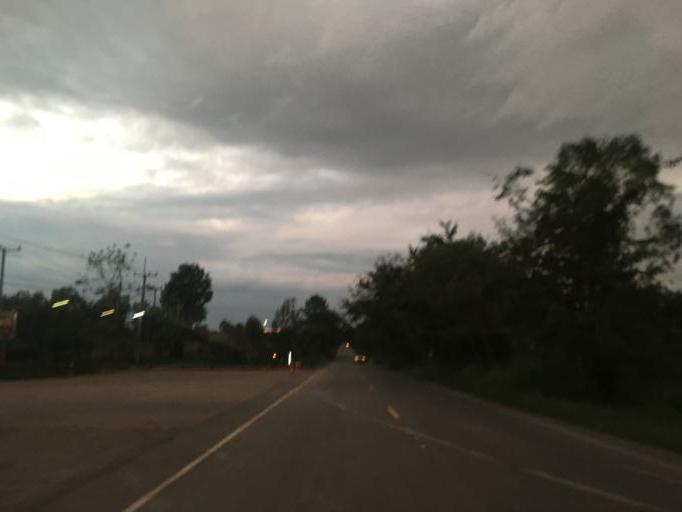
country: TH
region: Changwat Udon Thani
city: Nong Saeng
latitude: 17.2875
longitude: 102.7060
